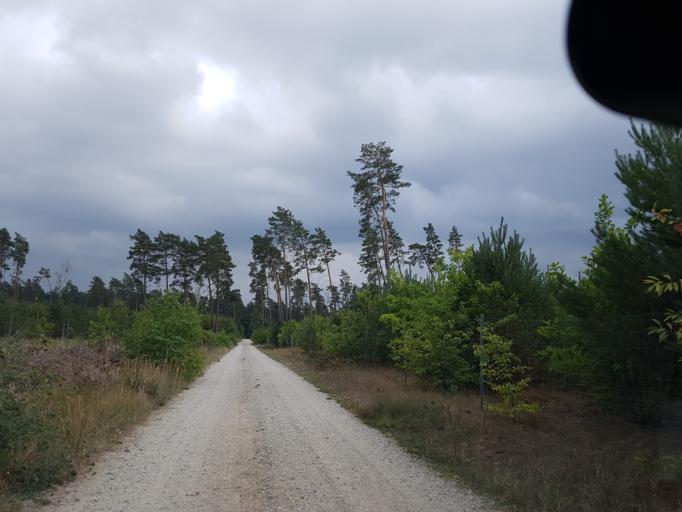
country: DE
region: Saxony-Anhalt
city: Rosslau
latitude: 52.0229
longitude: 12.2905
